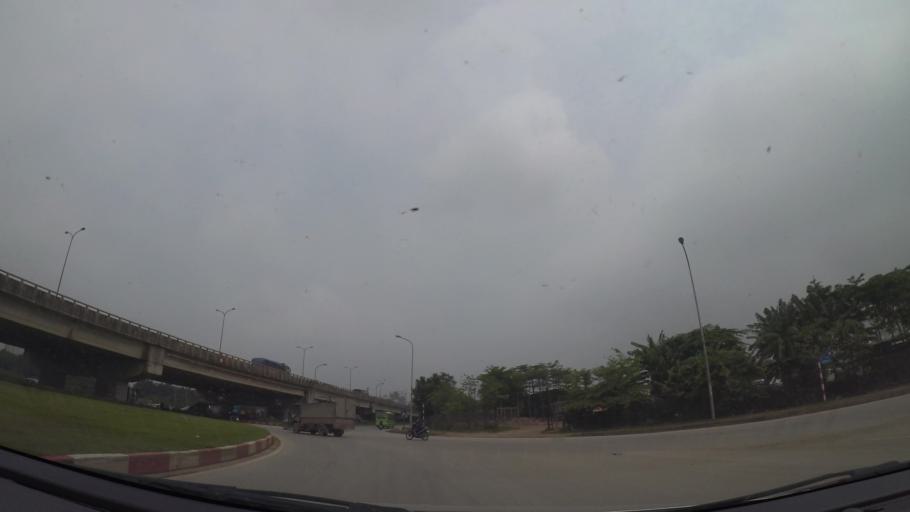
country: VN
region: Ha Noi
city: Tay Ho
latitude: 21.1257
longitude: 105.7816
